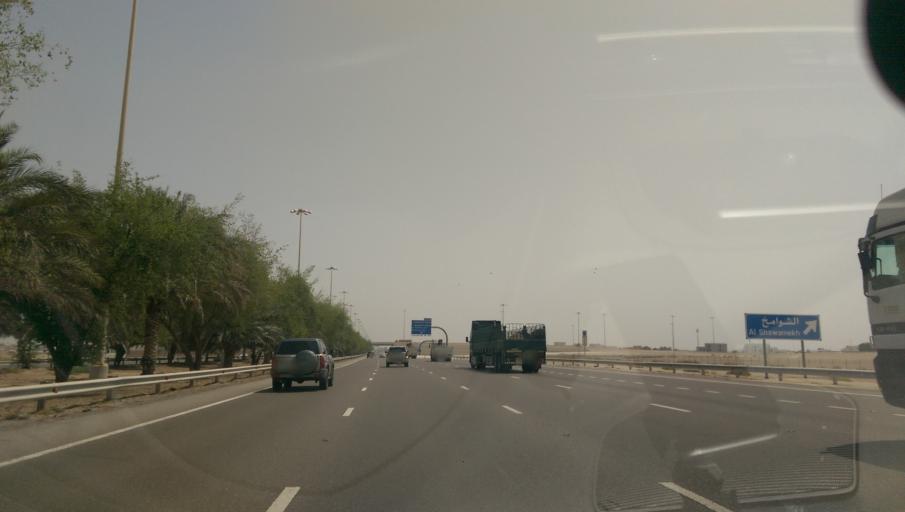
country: AE
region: Abu Dhabi
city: Abu Dhabi
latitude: 24.3639
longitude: 54.6522
